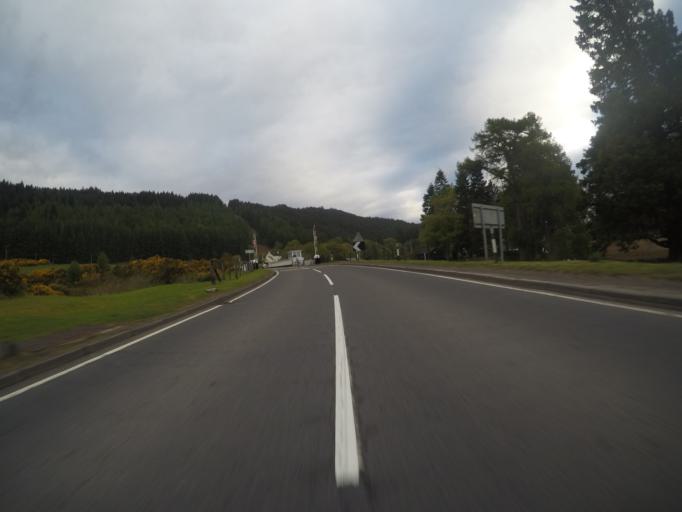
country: GB
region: Scotland
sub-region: Highland
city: Spean Bridge
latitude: 57.0438
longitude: -4.8038
